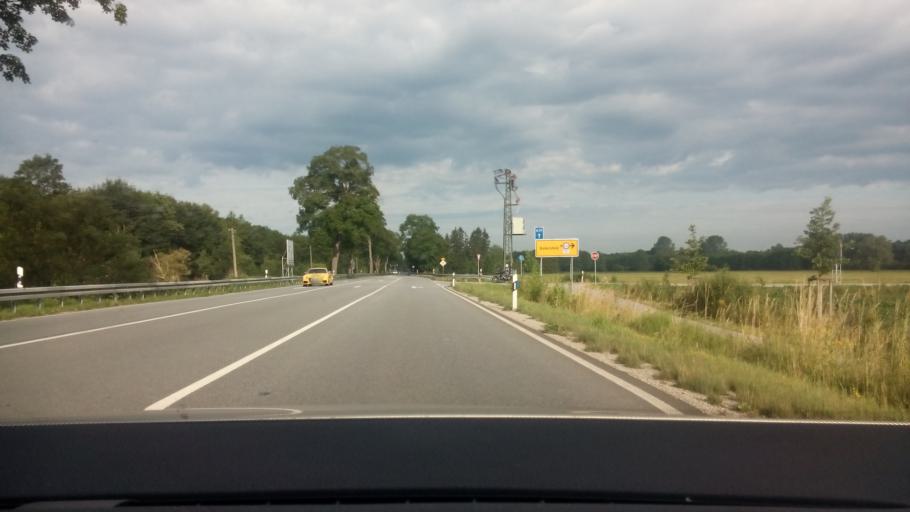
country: DE
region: Bavaria
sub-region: Upper Bavaria
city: Oberschleissheim
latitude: 48.2533
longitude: 11.5153
